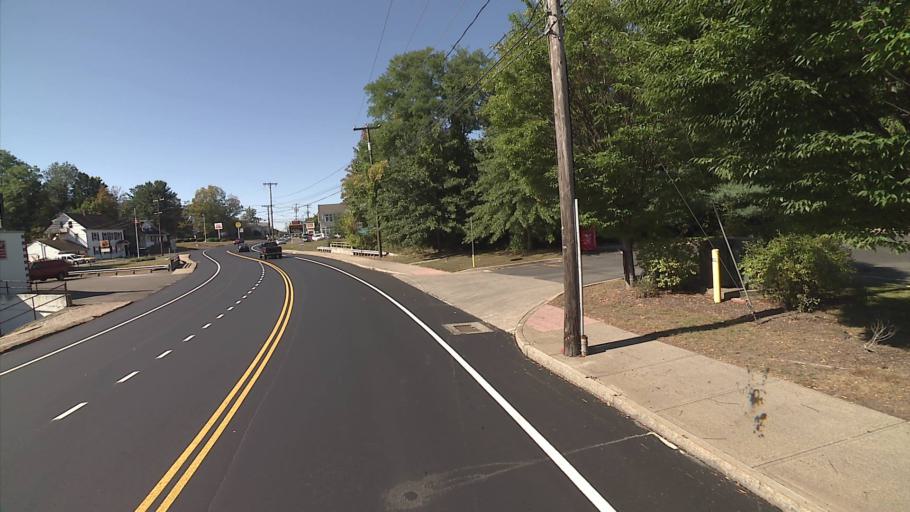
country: US
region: Connecticut
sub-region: Tolland County
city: Rockville
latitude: 41.8684
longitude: -72.4654
